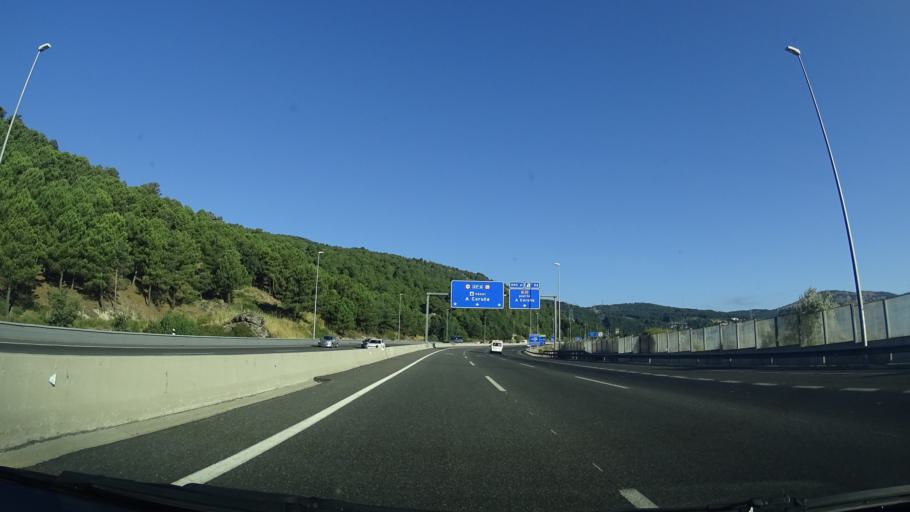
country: ES
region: Madrid
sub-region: Provincia de Madrid
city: Guadarrama
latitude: 40.6872
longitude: -4.1195
